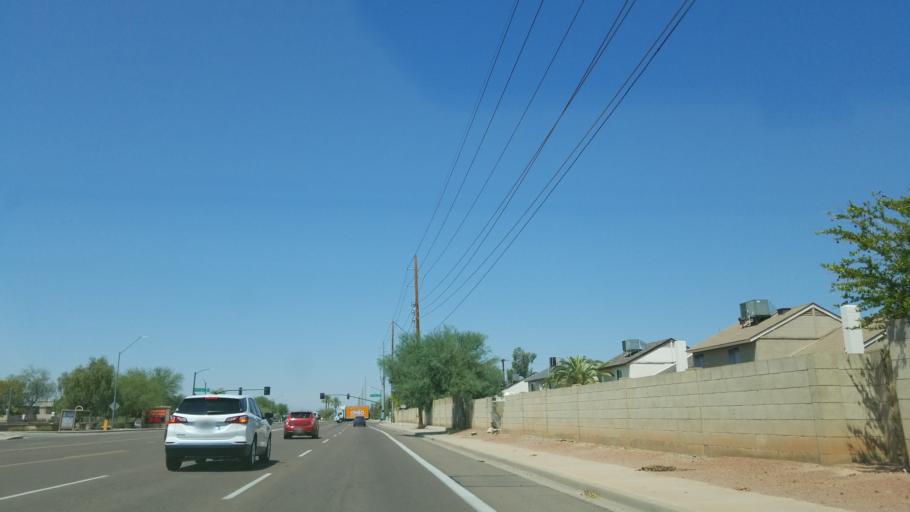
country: US
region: Arizona
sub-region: Maricopa County
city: Peoria
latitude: 33.6546
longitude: -112.1657
